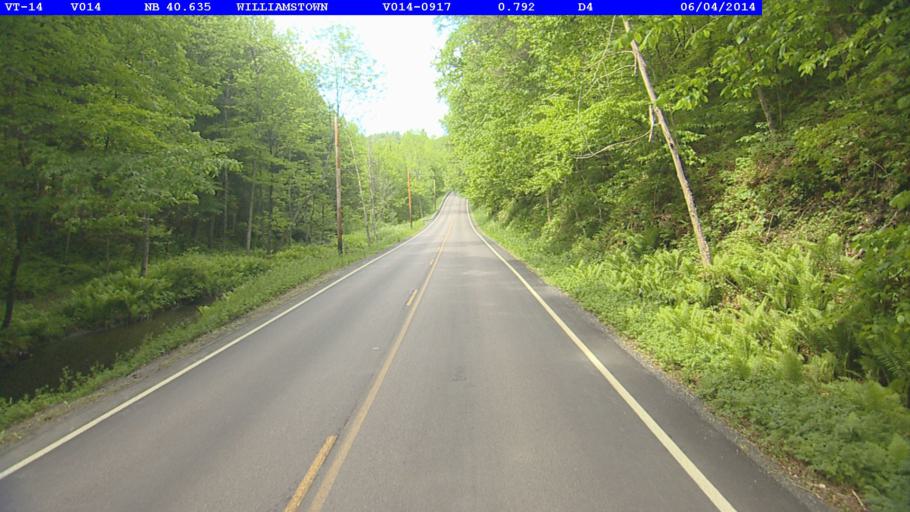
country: US
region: Vermont
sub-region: Orange County
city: Williamstown
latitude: 44.0815
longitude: -72.5713
